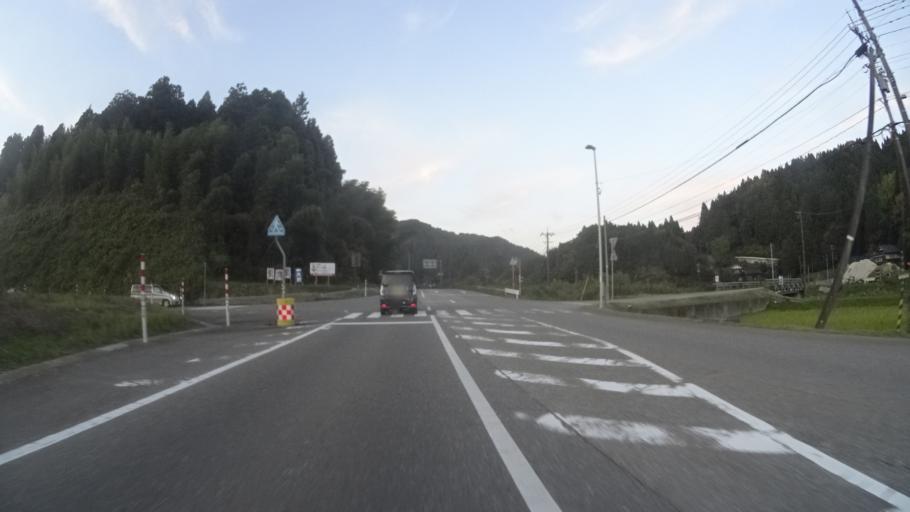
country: JP
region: Ishikawa
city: Nanao
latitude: 37.3083
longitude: 136.7980
